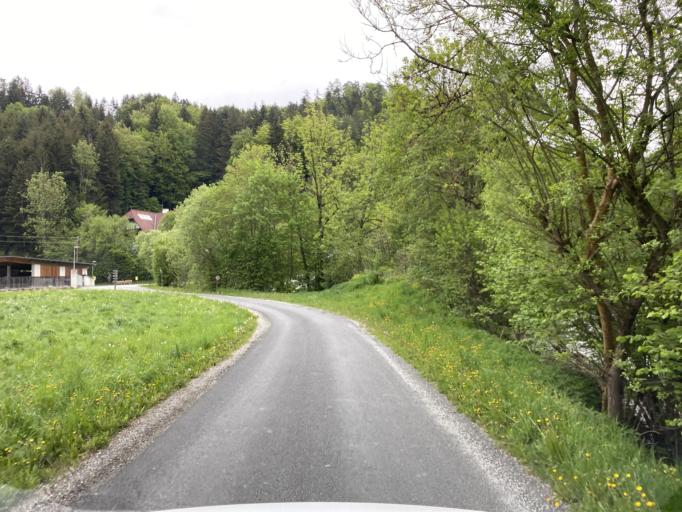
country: AT
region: Styria
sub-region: Politischer Bezirk Weiz
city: Koglhof
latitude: 47.3141
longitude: 15.6868
